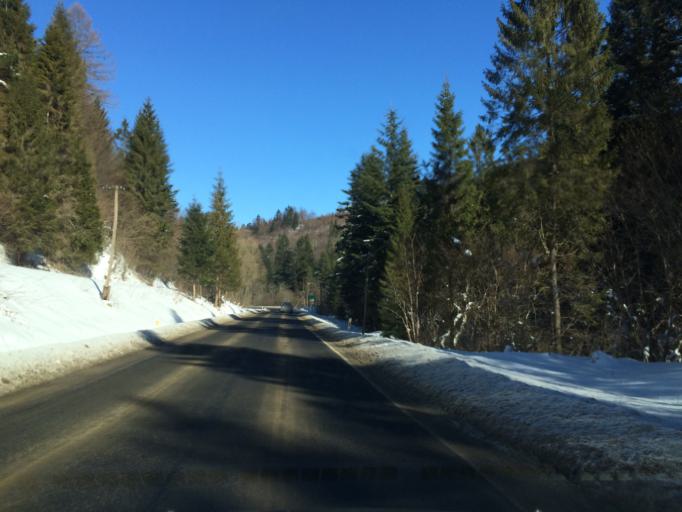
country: PL
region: Subcarpathian Voivodeship
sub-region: Powiat leski
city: Cisna
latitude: 49.2165
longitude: 22.3644
